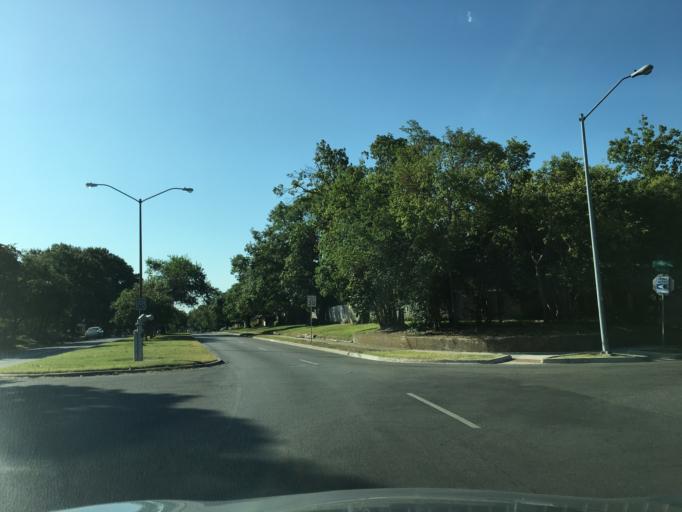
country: US
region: Texas
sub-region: Dallas County
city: Highland Park
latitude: 32.8608
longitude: -96.7099
